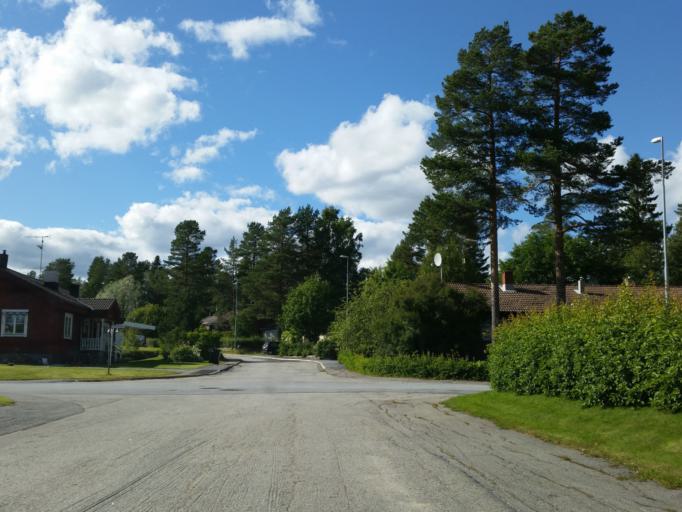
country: SE
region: Vaesterbotten
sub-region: Robertsfors Kommun
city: Robertsfors
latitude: 64.1979
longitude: 20.8434
